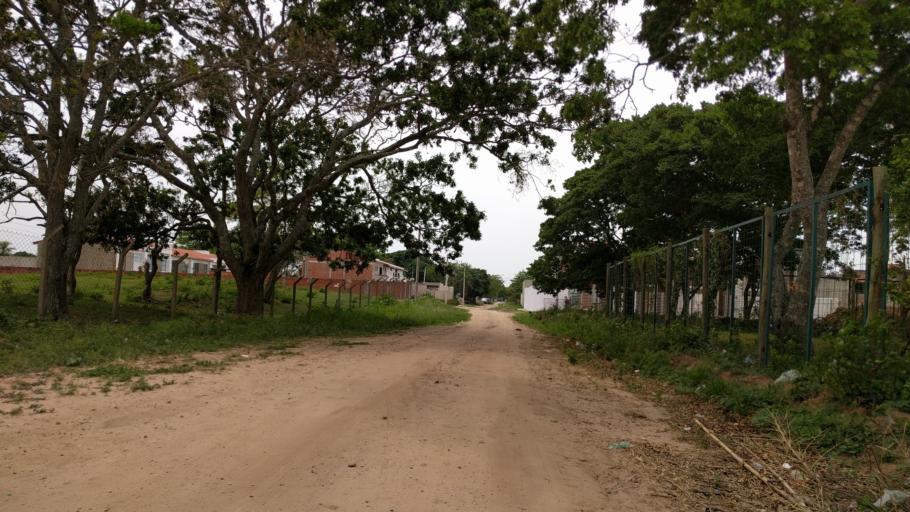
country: BO
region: Santa Cruz
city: Santa Cruz de la Sierra
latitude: -17.8164
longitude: -63.2339
